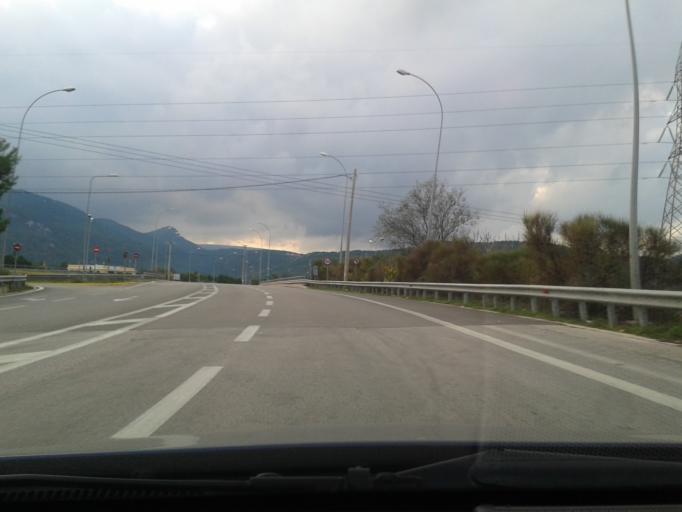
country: GR
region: Attica
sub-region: Nomarchia Anatolikis Attikis
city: Afidnes
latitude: 38.1889
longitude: 23.8525
